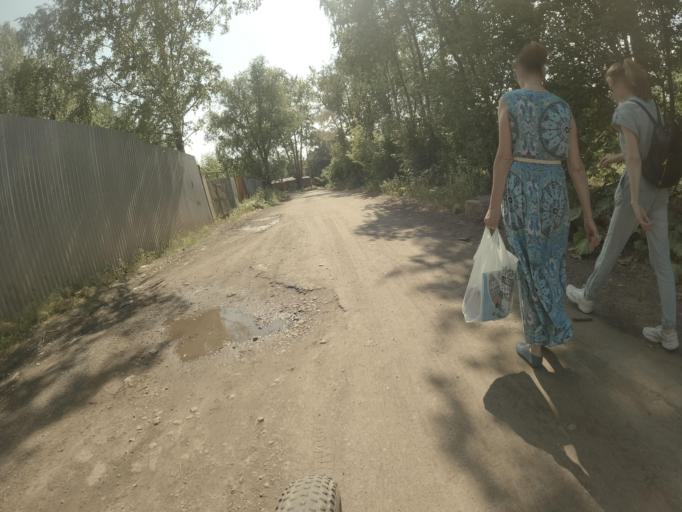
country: RU
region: St.-Petersburg
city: Obukhovo
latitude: 59.9098
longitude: 30.4347
